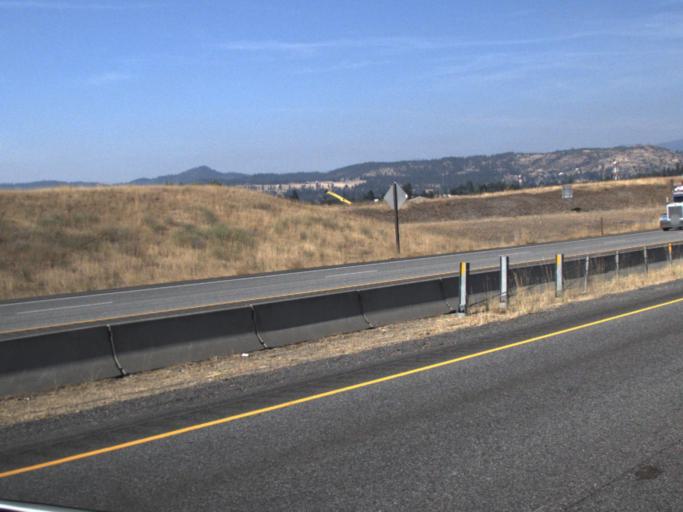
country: US
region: Washington
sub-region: Spokane County
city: Liberty Lake
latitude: 47.6746
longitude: -117.1066
